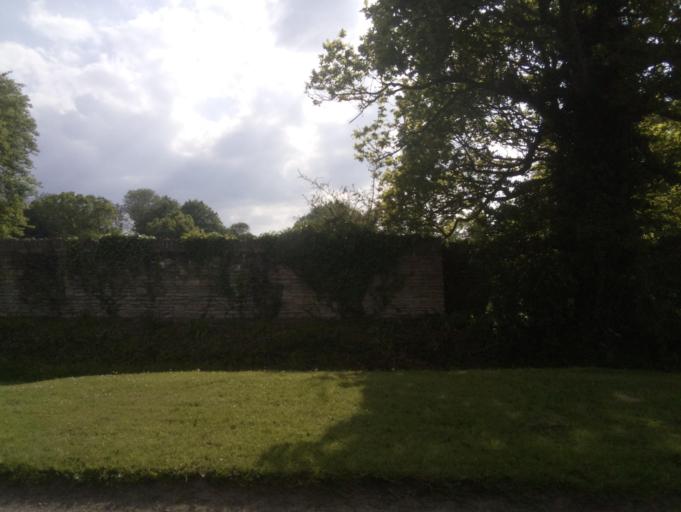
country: GB
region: England
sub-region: Wiltshire
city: Malmesbury
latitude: 51.5277
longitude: -2.0793
